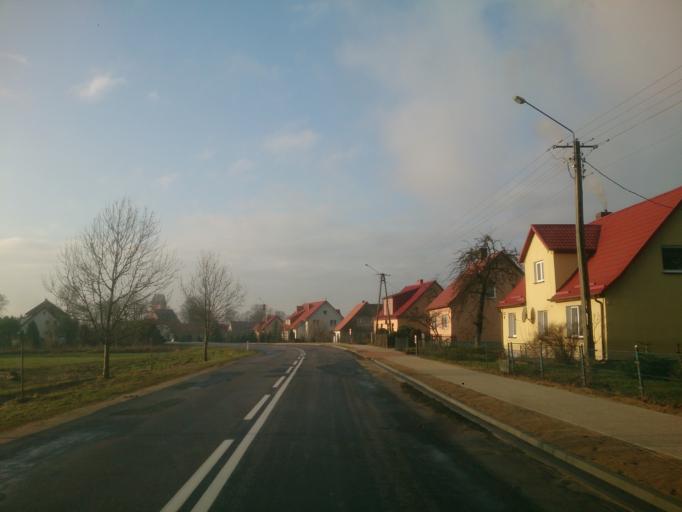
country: PL
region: Pomeranian Voivodeship
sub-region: Powiat bytowski
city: Tuchomie
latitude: 54.0614
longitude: 17.2446
